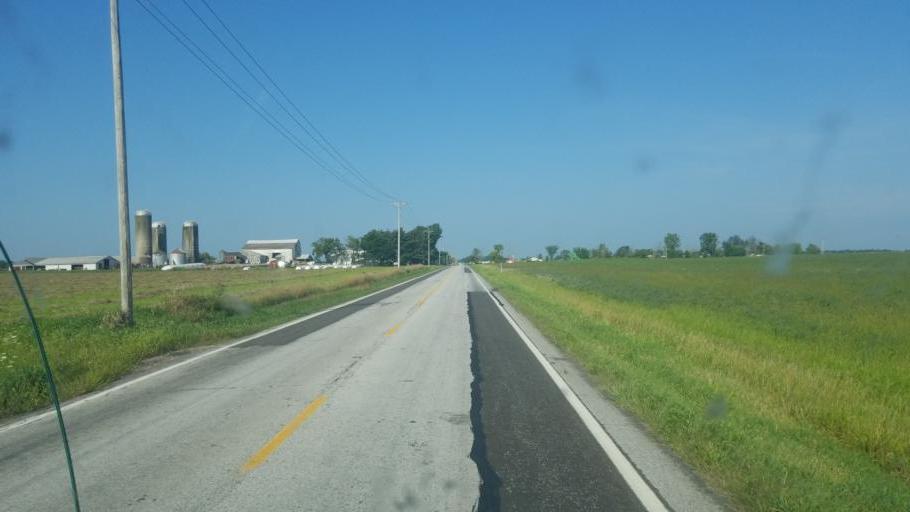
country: US
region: Ohio
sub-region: Lorain County
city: Wellington
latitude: 41.1003
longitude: -82.1376
